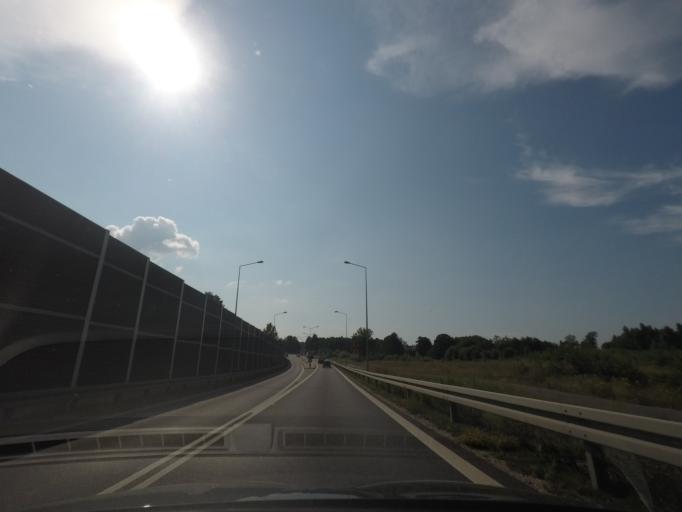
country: PL
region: Silesian Voivodeship
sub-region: Powiat pszczynski
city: Czarkow
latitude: 50.0018
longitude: 18.9126
